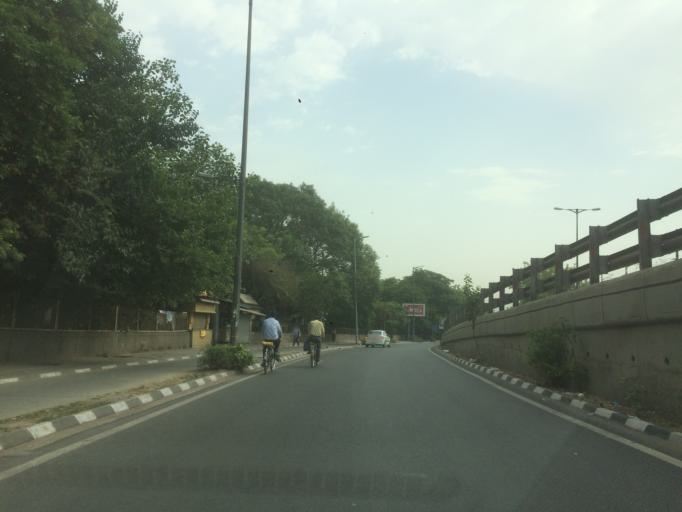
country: IN
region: NCT
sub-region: New Delhi
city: New Delhi
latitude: 28.5674
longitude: 77.2343
